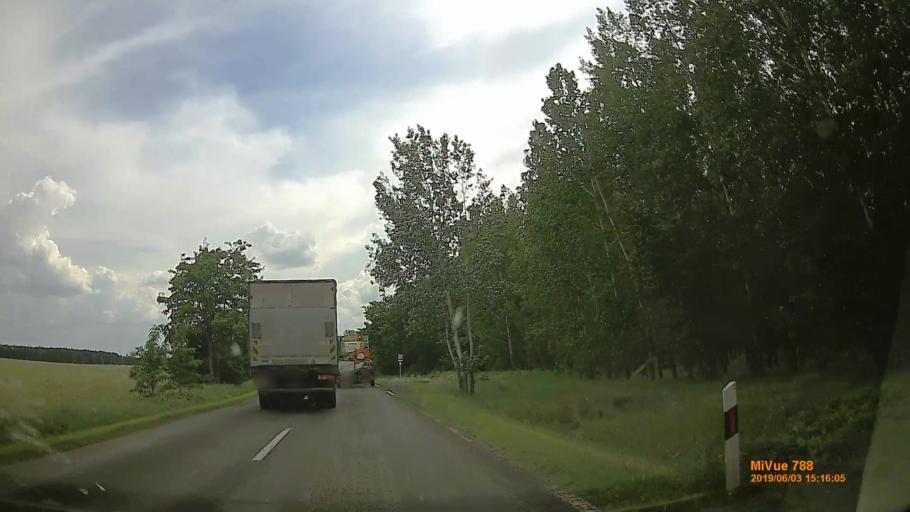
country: HU
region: Bacs-Kiskun
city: Orgovany
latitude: 46.7162
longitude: 19.5497
